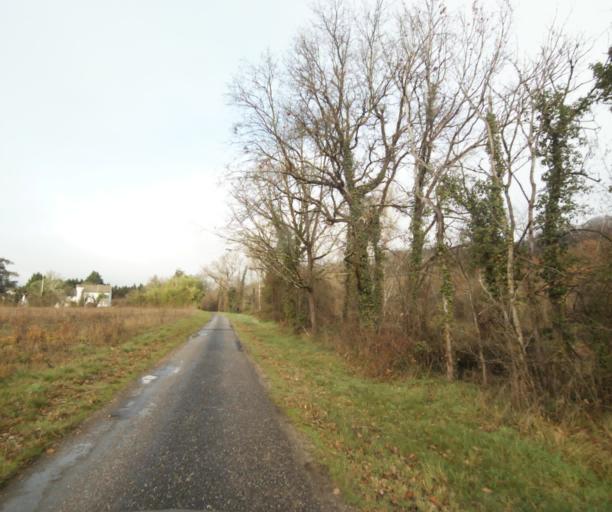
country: FR
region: Midi-Pyrenees
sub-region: Departement du Tarn-et-Garonne
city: Nohic
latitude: 43.8949
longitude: 1.4728
